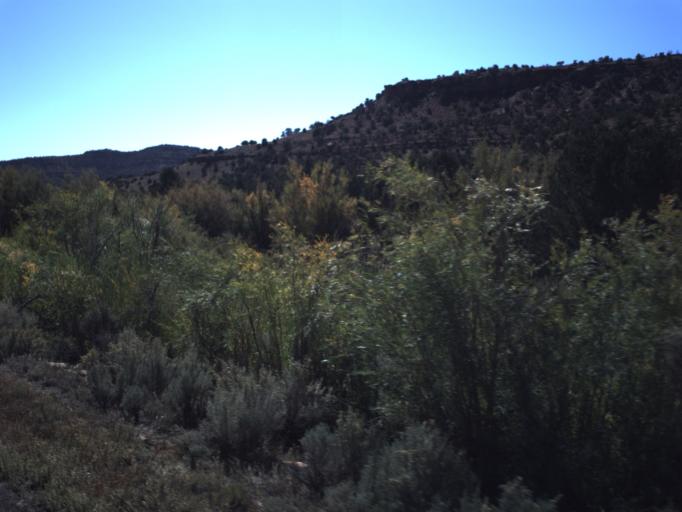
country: US
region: Utah
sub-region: Wayne County
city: Loa
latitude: 38.2806
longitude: -111.3891
